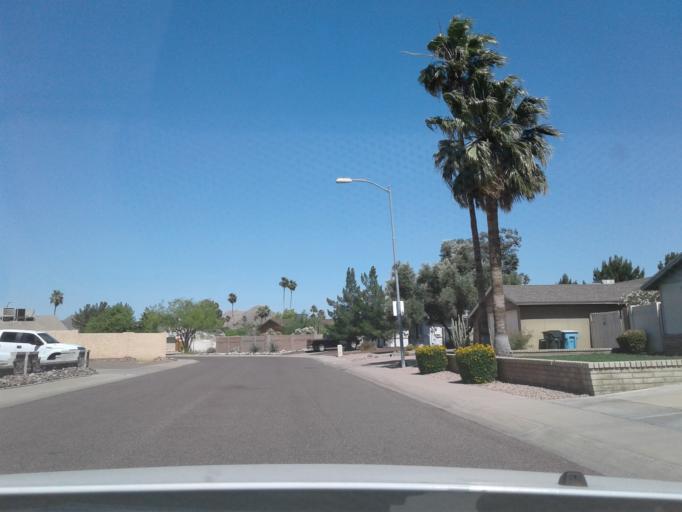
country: US
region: Arizona
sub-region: Maricopa County
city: Paradise Valley
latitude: 33.6018
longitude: -112.0035
